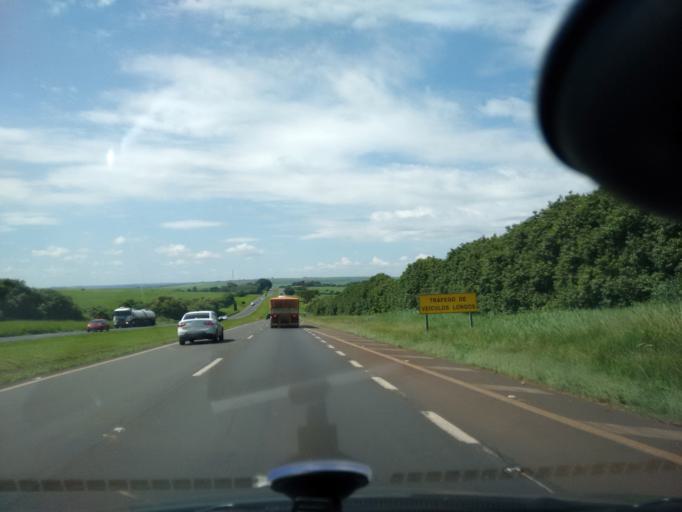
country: BR
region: Sao Paulo
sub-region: Araraquara
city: Araraquara
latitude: -21.8655
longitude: -48.1131
